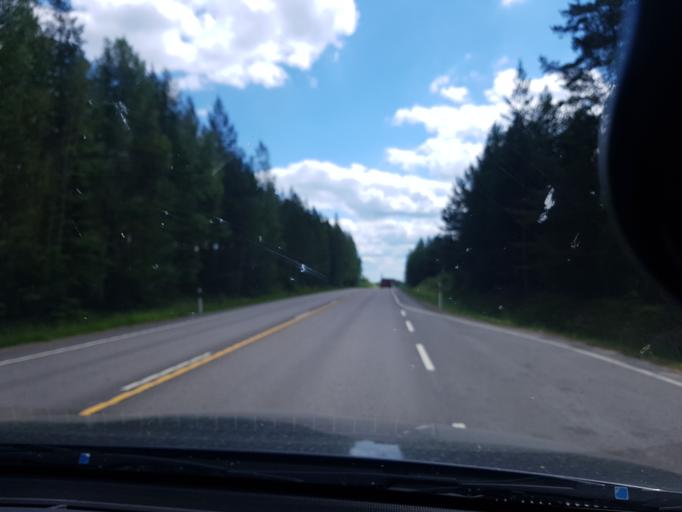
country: FI
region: Haeme
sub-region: Haemeenlinna
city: Parola
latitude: 61.1339
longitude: 24.4174
